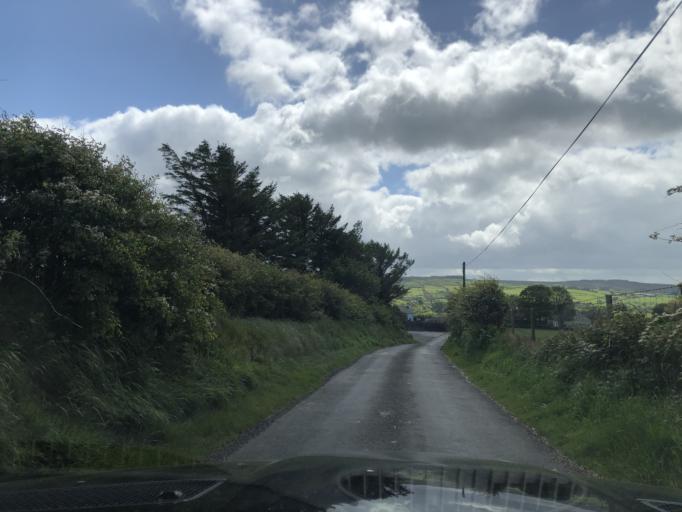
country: GB
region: Northern Ireland
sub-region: Moyle District
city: Ballycastle
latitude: 55.2029
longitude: -6.1723
